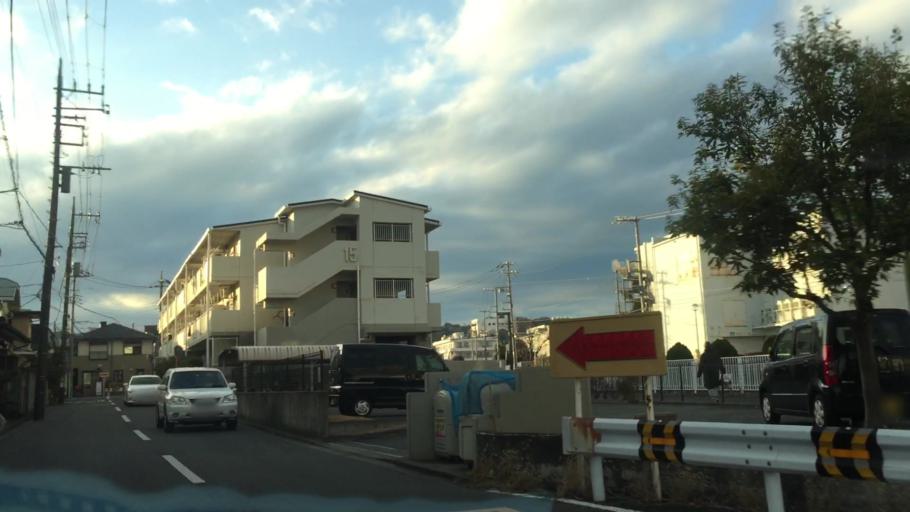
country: JP
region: Kanagawa
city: Zushi
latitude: 35.3431
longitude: 139.6166
